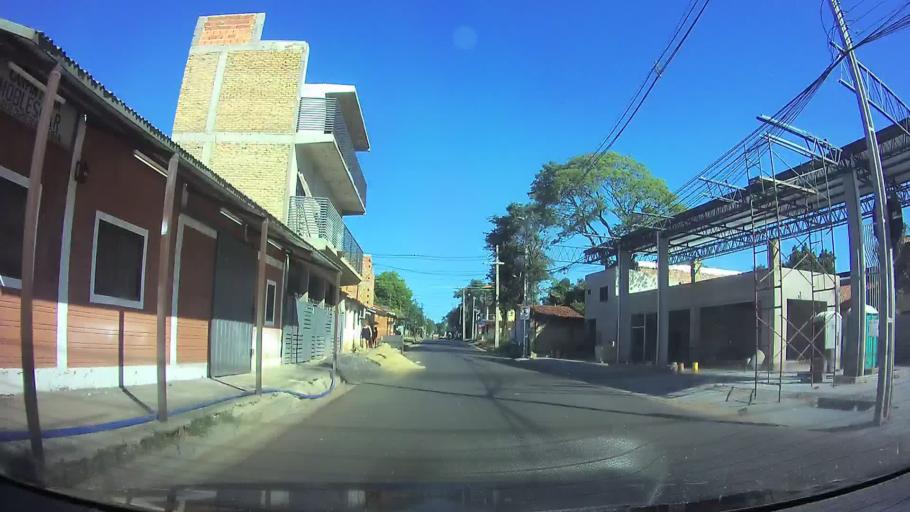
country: PY
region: Central
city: Fernando de la Mora
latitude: -25.2928
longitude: -57.5403
